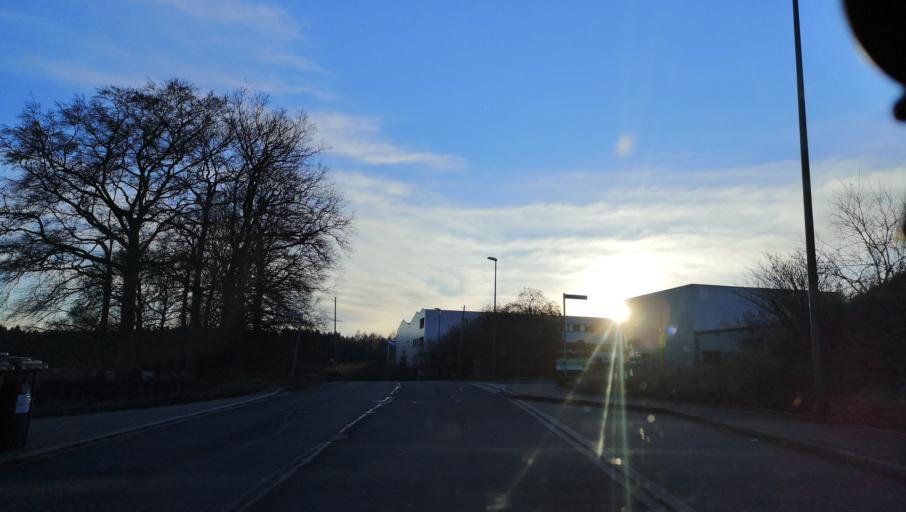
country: DE
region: North Rhine-Westphalia
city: Radevormwald
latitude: 51.1970
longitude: 7.3847
